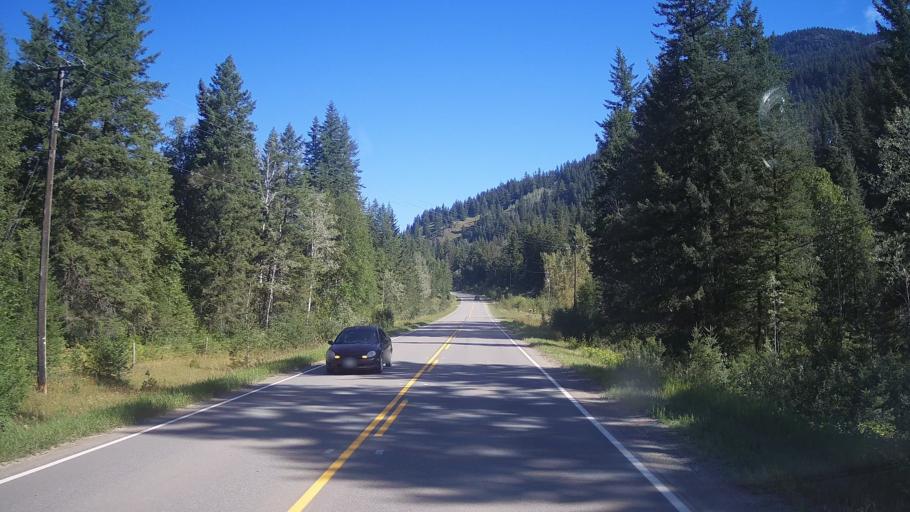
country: CA
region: British Columbia
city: Kamloops
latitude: 51.4435
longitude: -120.2122
